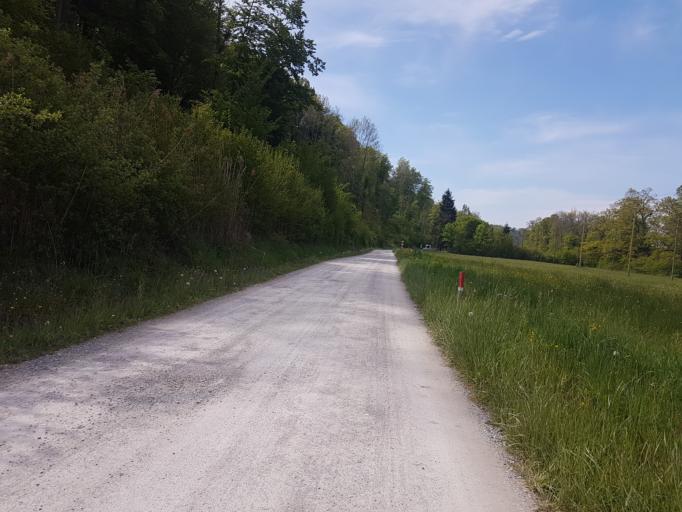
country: CH
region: Bern
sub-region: Seeland District
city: Tauffelen
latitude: 47.0725
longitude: 7.1930
